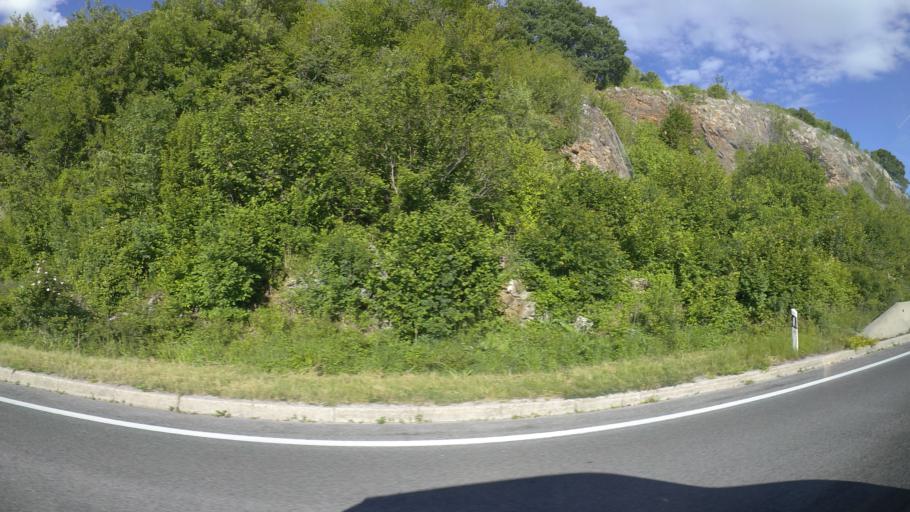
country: BA
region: Federation of Bosnia and Herzegovina
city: Bihac
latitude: 44.6192
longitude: 15.7367
